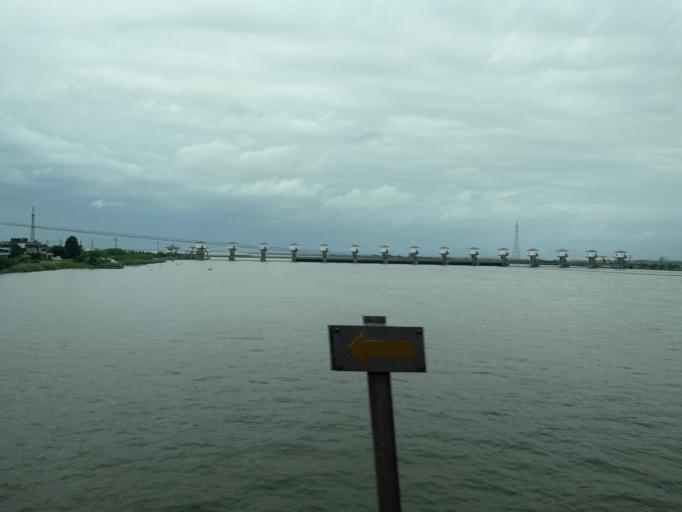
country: JP
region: Akita
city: Tenno
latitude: 39.9024
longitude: 139.9571
